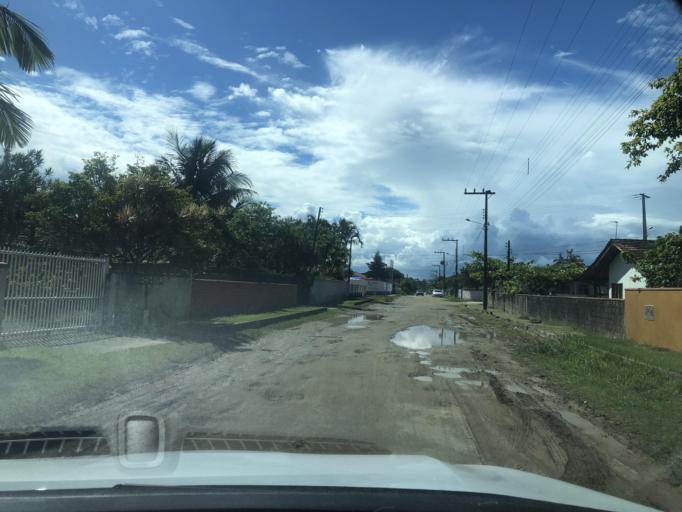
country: BR
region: Santa Catarina
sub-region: Sao Francisco Do Sul
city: Sao Francisco do Sul
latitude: -26.2154
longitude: -48.5279
